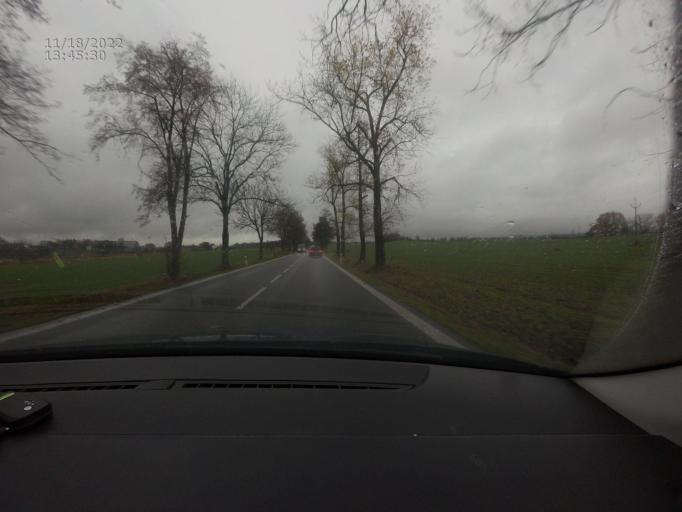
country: CZ
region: Jihocesky
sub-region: Okres Strakonice
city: Blatna
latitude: 49.4281
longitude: 13.8484
